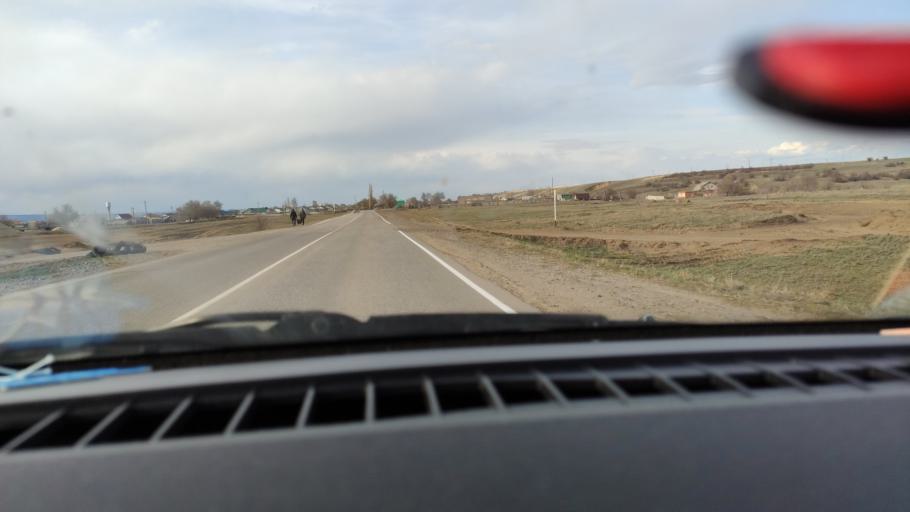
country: RU
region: Saratov
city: Privolzhskiy
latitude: 51.1989
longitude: 45.9158
